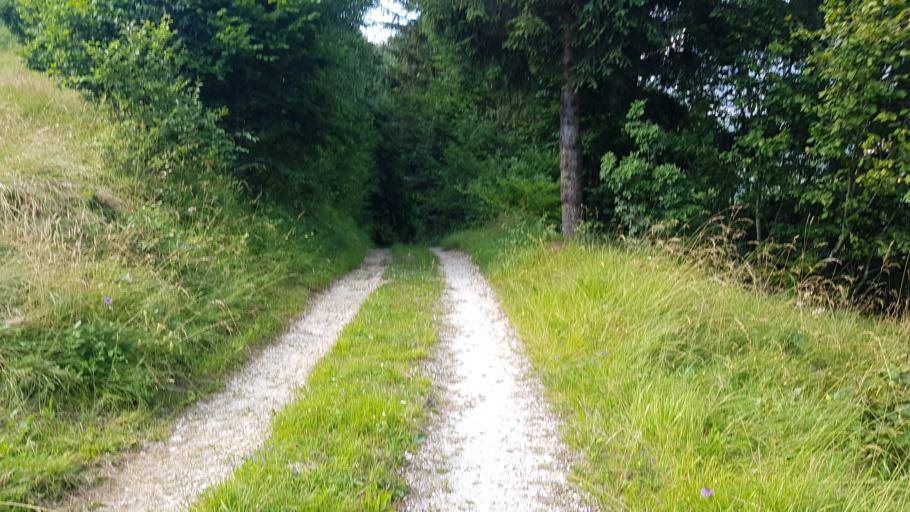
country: IT
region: Friuli Venezia Giulia
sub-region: Provincia di Udine
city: Dogna
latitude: 46.4301
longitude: 13.3058
